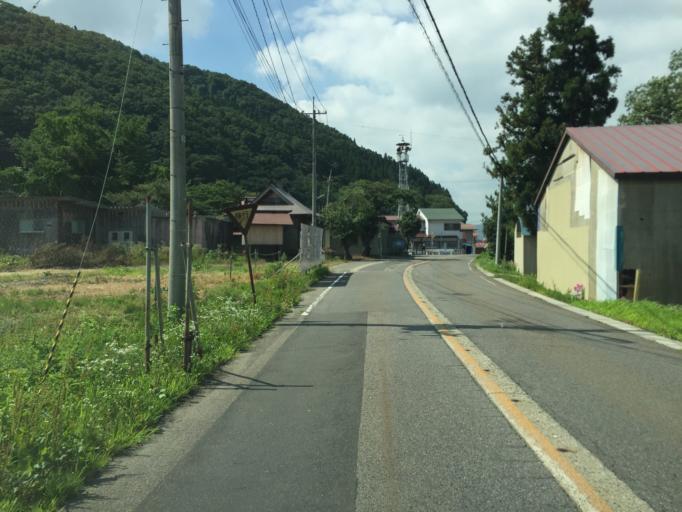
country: JP
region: Fukushima
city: Inawashiro
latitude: 37.4396
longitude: 140.1505
